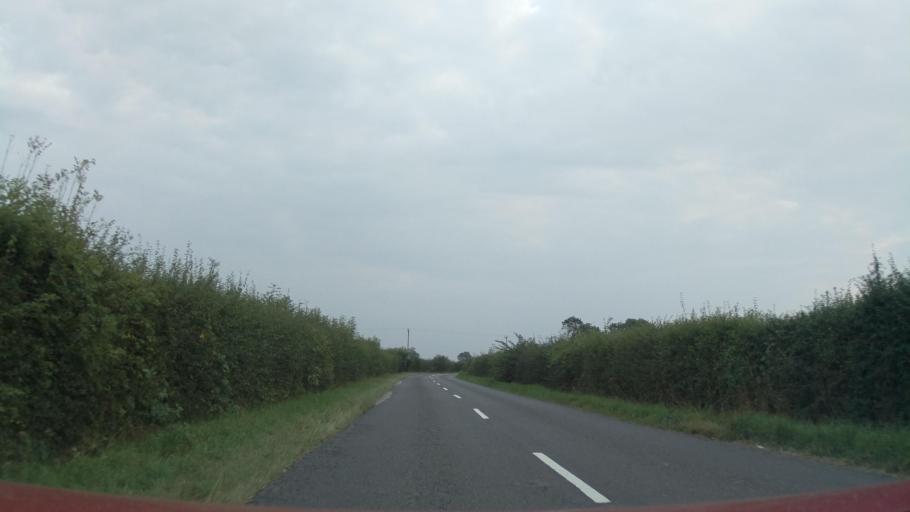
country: GB
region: England
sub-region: Lincolnshire
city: Skellingthorpe
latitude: 53.1363
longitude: -0.6455
